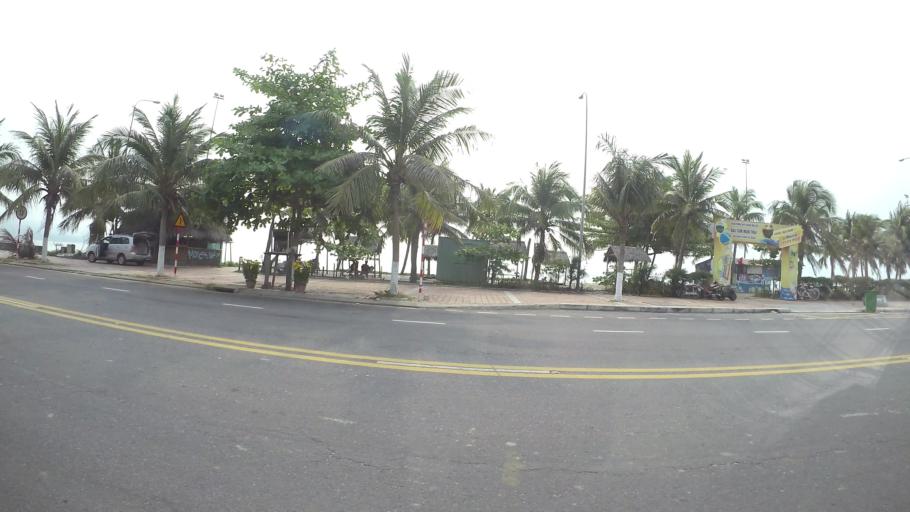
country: VN
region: Da Nang
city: Son Tra
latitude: 16.0901
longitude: 108.2499
